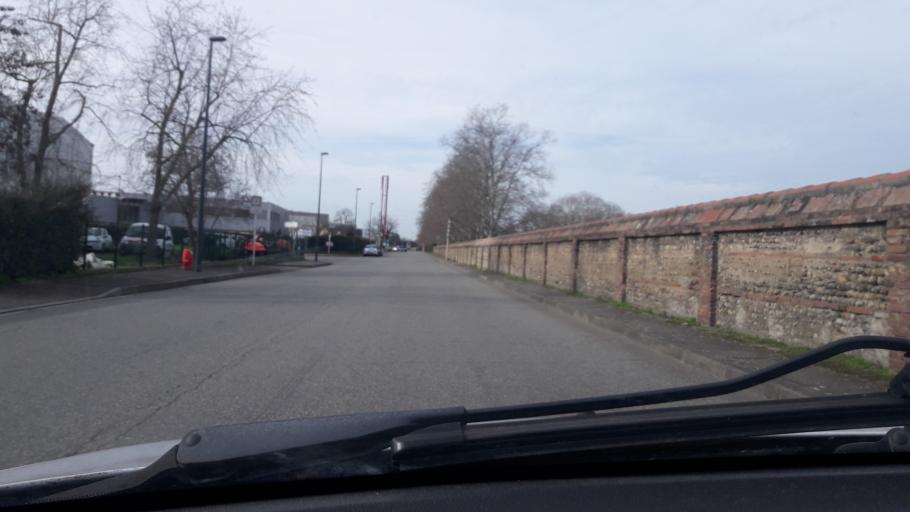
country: FR
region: Midi-Pyrenees
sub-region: Departement de la Haute-Garonne
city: Portet-sur-Garonne
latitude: 43.5563
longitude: 1.4217
